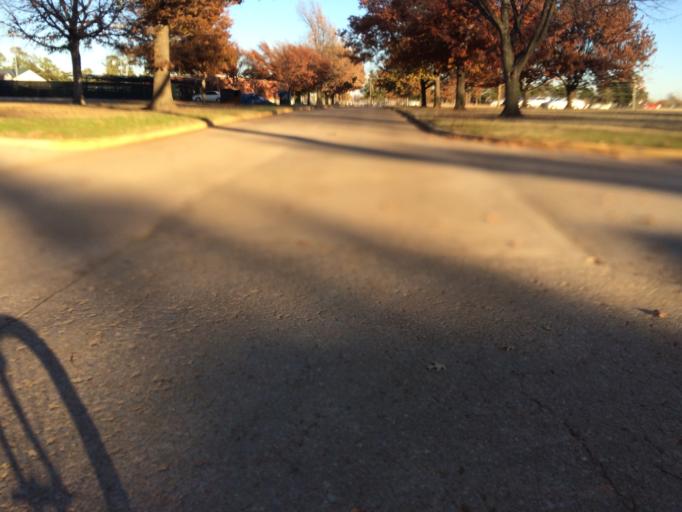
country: US
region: Oklahoma
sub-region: Cleveland County
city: Norman
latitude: 35.1944
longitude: -97.4437
